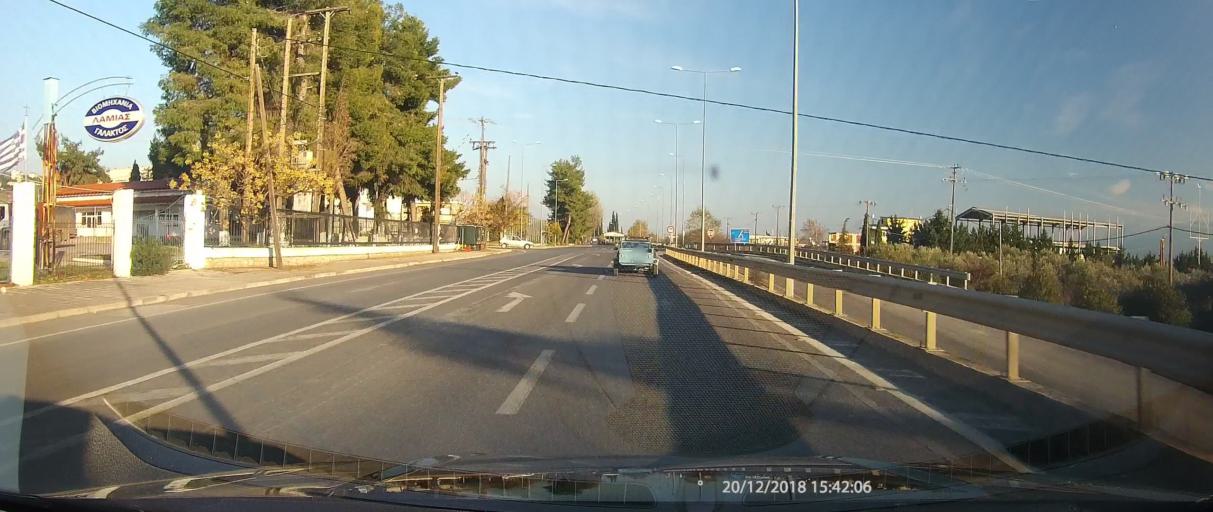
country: GR
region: Central Greece
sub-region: Nomos Fthiotidos
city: Stavros
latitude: 38.8893
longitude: 22.3947
